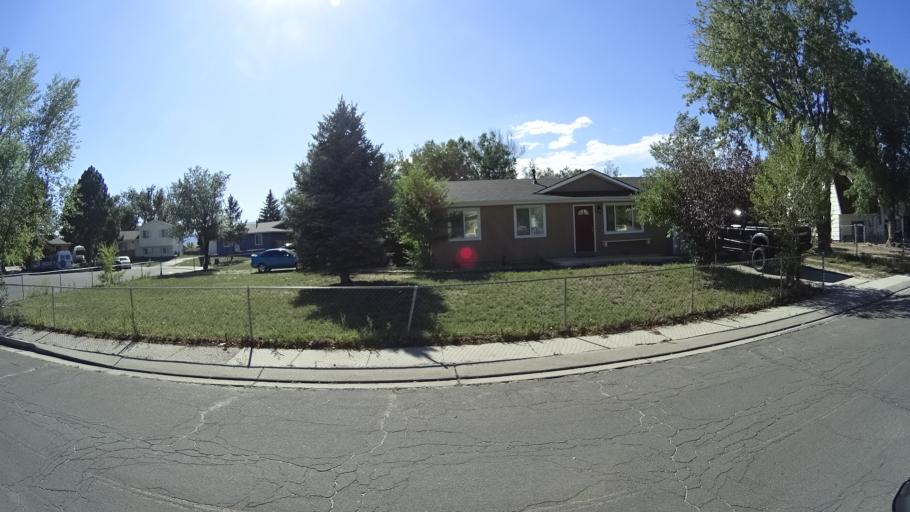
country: US
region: Colorado
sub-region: El Paso County
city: Stratmoor
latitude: 38.7960
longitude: -104.7480
